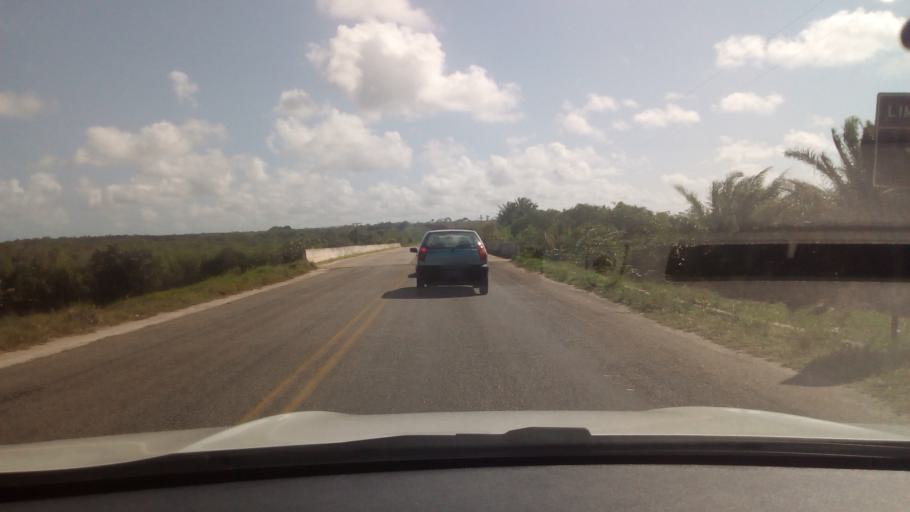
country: BR
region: Paraiba
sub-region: Conde
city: Conde
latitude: -7.2278
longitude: -34.8412
